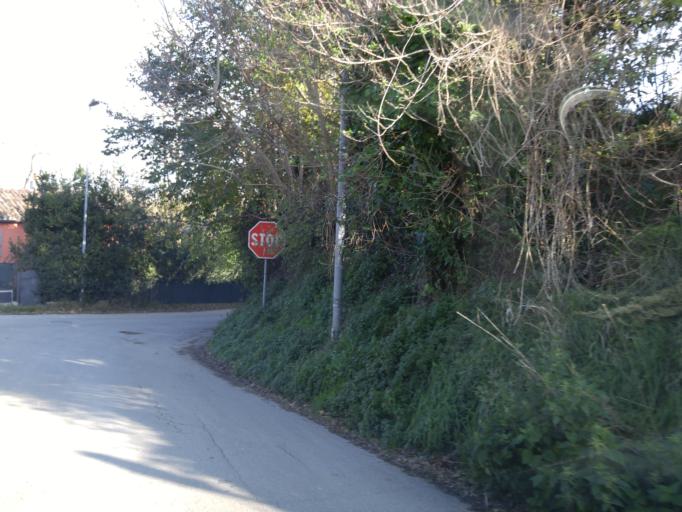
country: IT
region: The Marches
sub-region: Provincia di Pesaro e Urbino
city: Fenile
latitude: 43.8240
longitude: 12.9325
